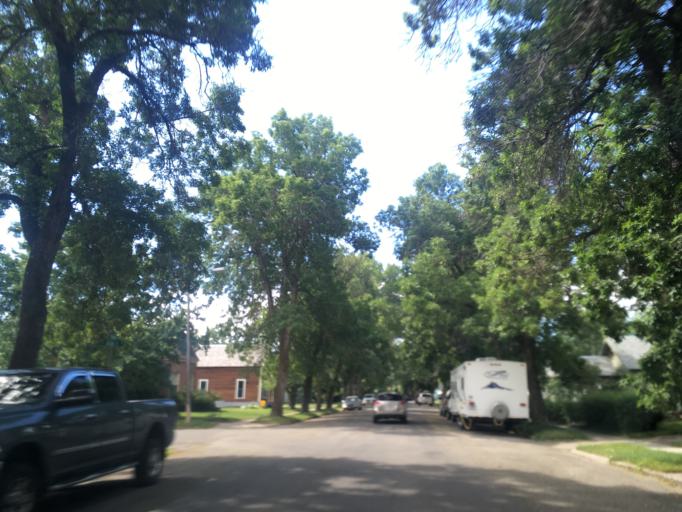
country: US
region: Montana
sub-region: Gallatin County
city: Bozeman
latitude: 45.6829
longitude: -111.0303
